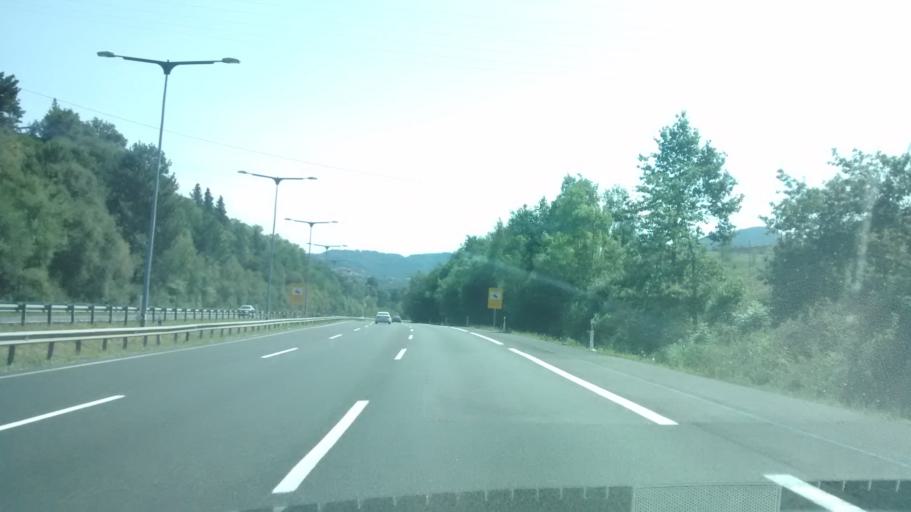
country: ES
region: Basque Country
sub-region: Bizkaia
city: Arrigorriaga
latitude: 43.2171
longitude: -2.9047
